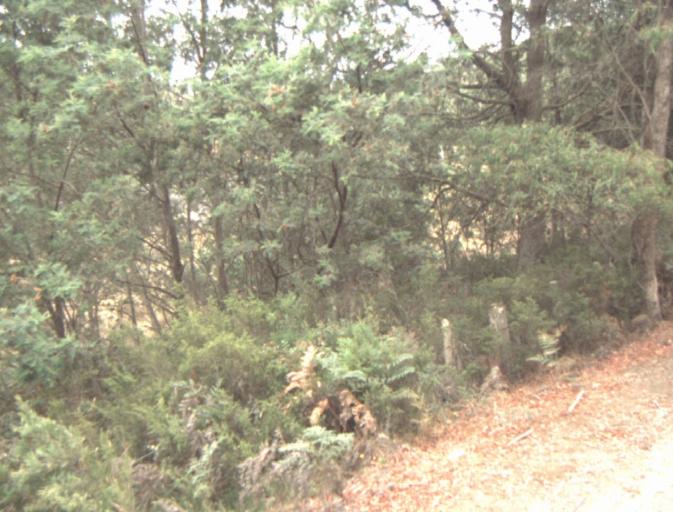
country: AU
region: Tasmania
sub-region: Northern Midlands
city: Evandale
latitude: -41.4604
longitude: 147.4954
